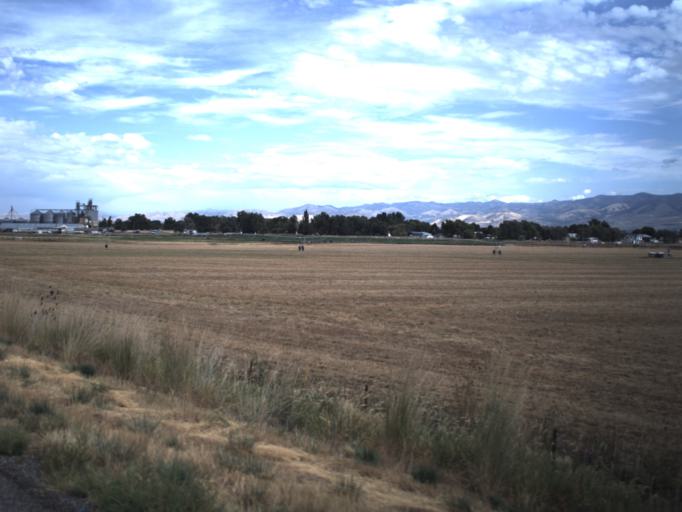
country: US
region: Utah
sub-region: Cache County
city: Lewiston
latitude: 41.9107
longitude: -111.9527
